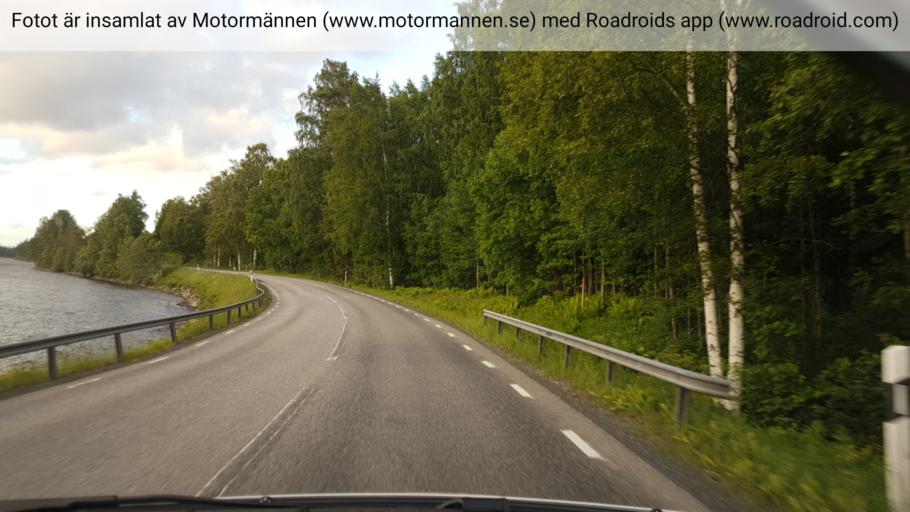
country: SE
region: OErebro
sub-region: Nora Kommun
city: As
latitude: 59.4892
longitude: 14.9382
